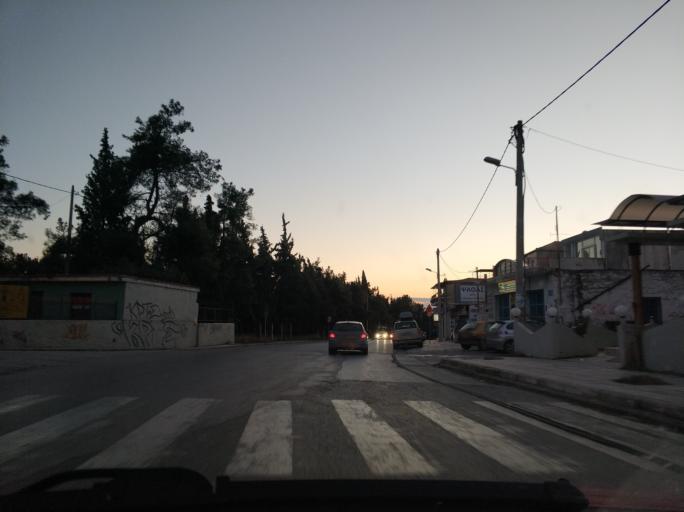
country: GR
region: Central Macedonia
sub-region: Nomos Thessalonikis
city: Stavroupoli
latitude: 40.6755
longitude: 22.9450
